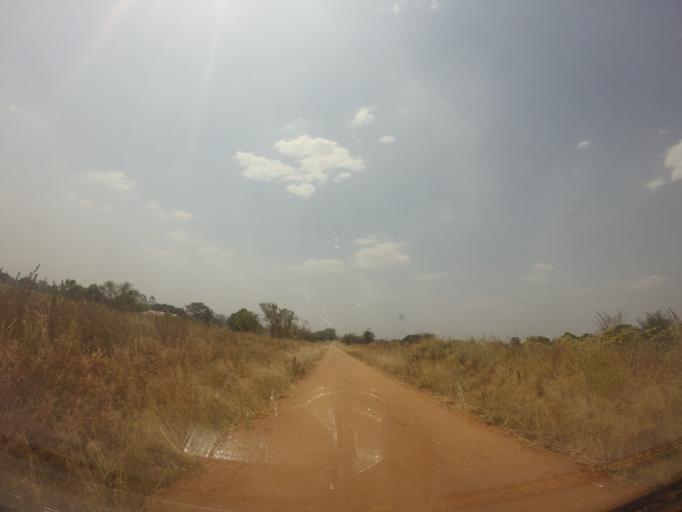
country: UG
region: Northern Region
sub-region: Arua District
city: Arua
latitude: 2.8844
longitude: 31.2077
